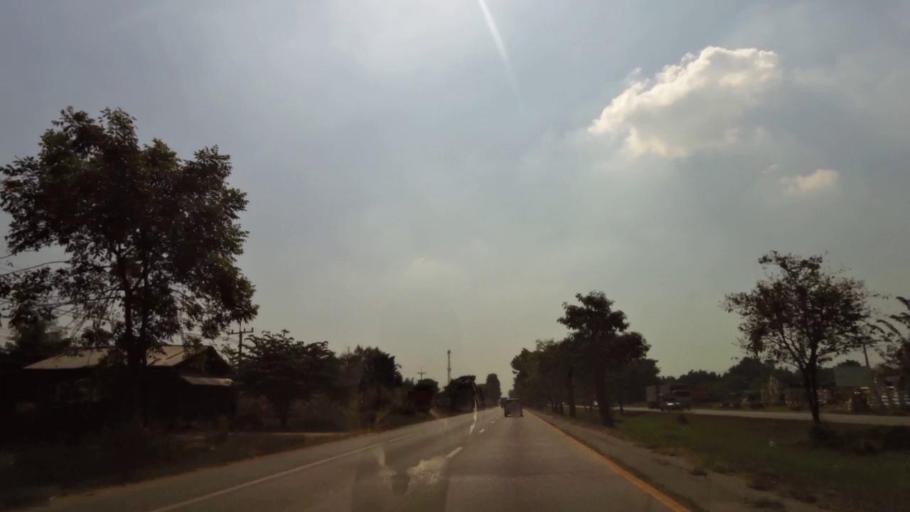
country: TH
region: Phichit
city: Wachira Barami
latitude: 16.5357
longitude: 100.1441
